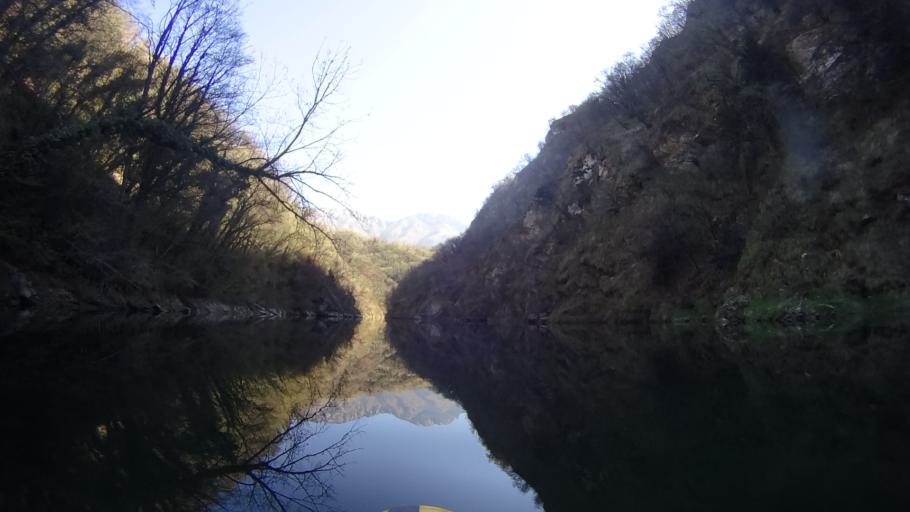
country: IT
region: Veneto
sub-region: Provincia di Vicenza
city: Cogollo del Cengio
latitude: 45.7768
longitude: 11.4098
